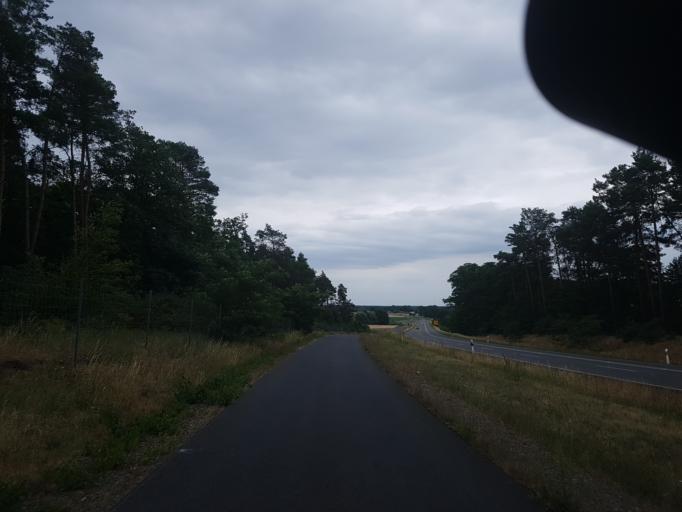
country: DE
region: Brandenburg
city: Falkenberg
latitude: 51.6447
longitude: 13.3027
